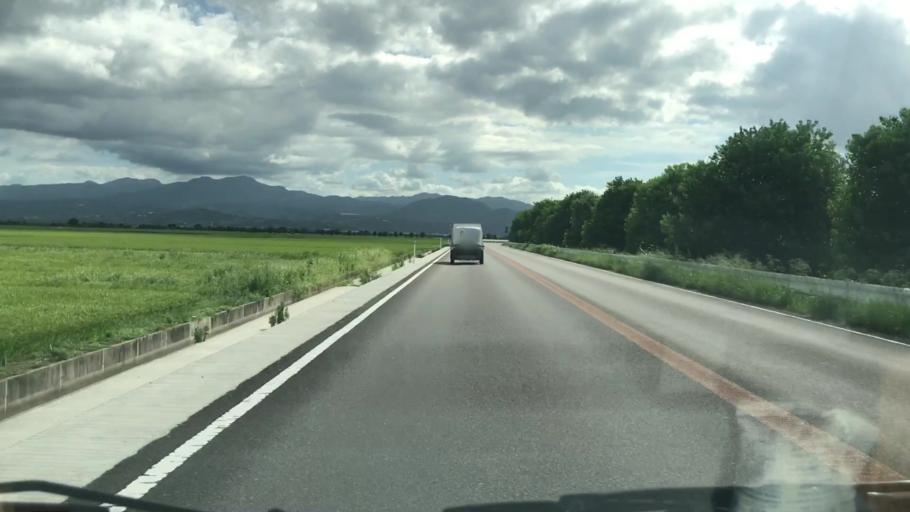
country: JP
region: Saga Prefecture
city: Kashima
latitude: 33.1400
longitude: 130.1437
